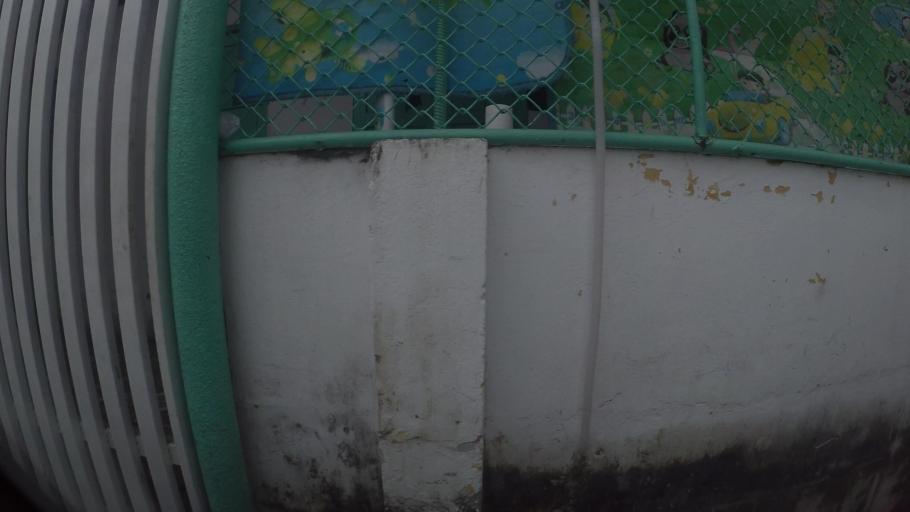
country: VN
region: Da Nang
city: Son Tra
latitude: 16.0451
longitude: 108.2453
